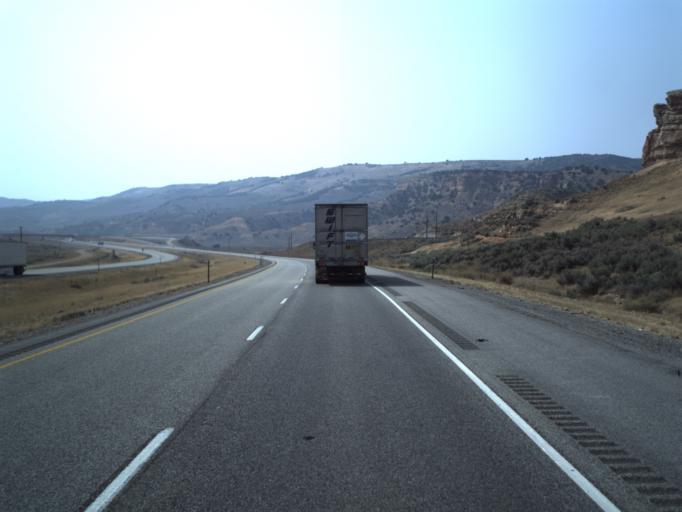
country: US
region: Wyoming
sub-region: Uinta County
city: Evanston
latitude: 41.1239
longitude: -111.1761
